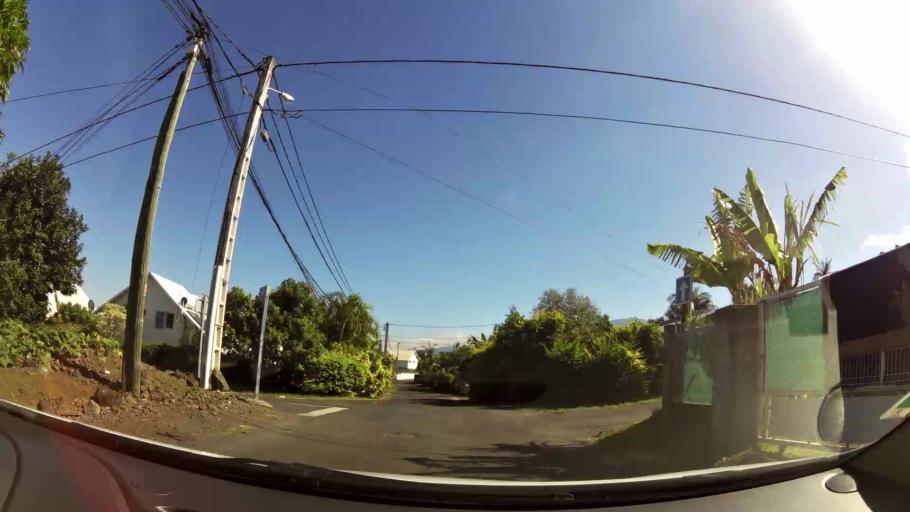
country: RE
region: Reunion
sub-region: Reunion
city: Le Tampon
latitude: -21.2669
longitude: 55.5011
